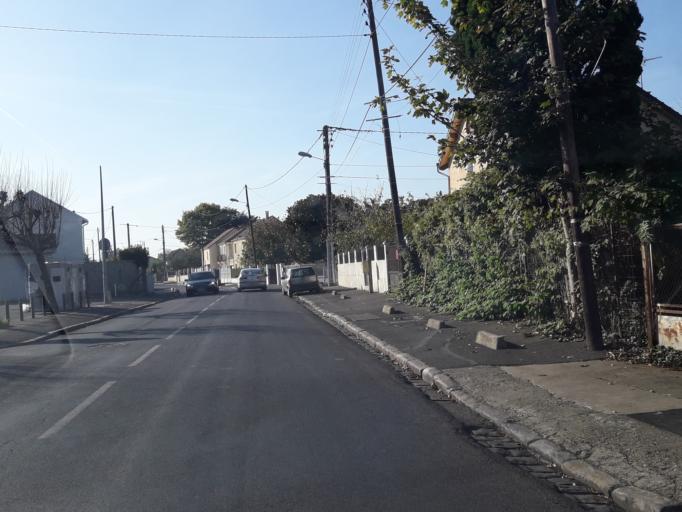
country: FR
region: Ile-de-France
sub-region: Departement de l'Essonne
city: Morsang-sur-Orge
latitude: 48.6521
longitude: 2.3562
